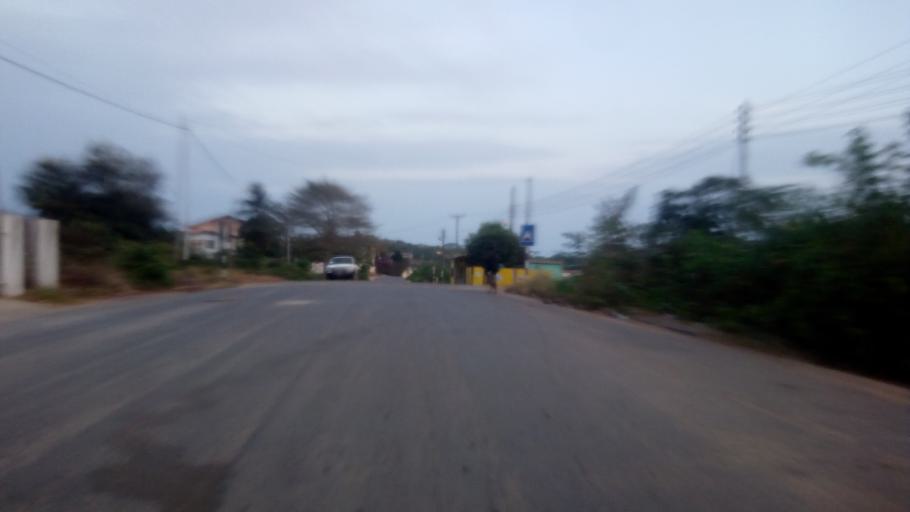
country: GH
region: Central
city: Cape Coast
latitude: 5.1165
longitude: -1.2710
